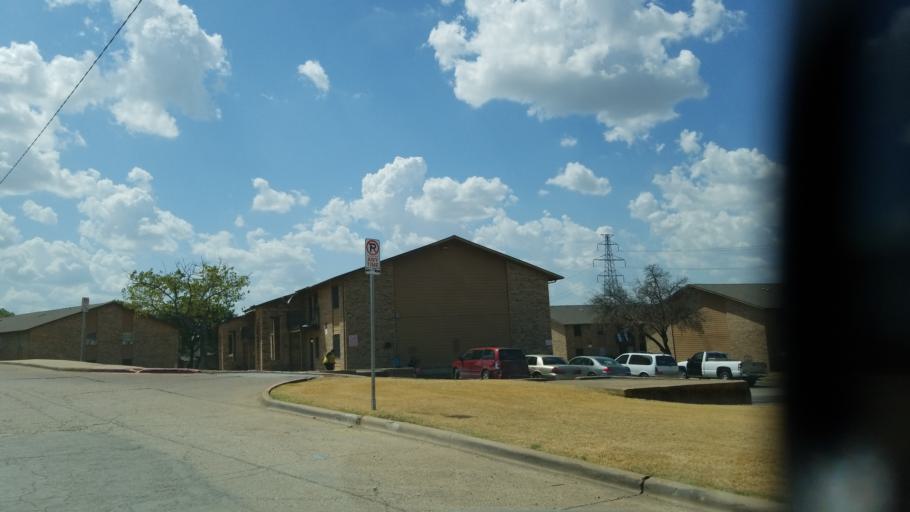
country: US
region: Texas
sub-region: Dallas County
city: Cockrell Hill
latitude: 32.7412
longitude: -96.9123
